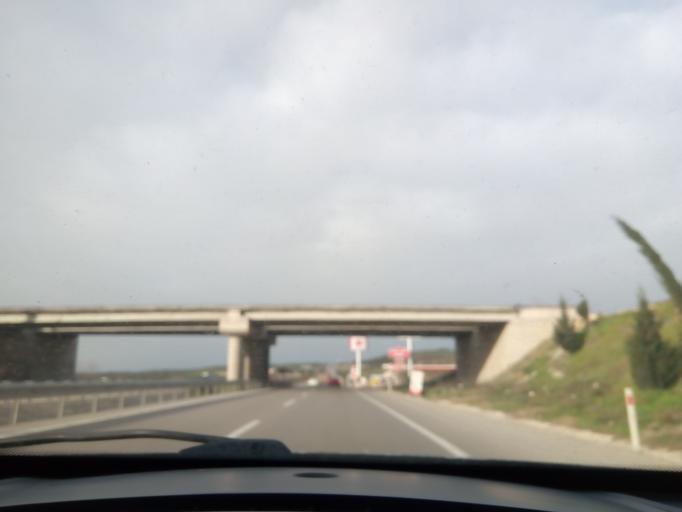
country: TR
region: Bursa
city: Gorukle
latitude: 40.2140
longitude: 28.7107
